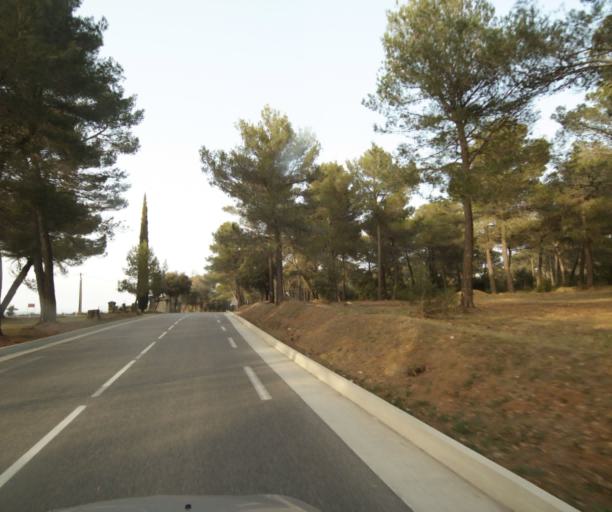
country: FR
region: Provence-Alpes-Cote d'Azur
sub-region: Departement des Bouches-du-Rhone
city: Rognes
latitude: 43.6260
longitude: 5.3494
